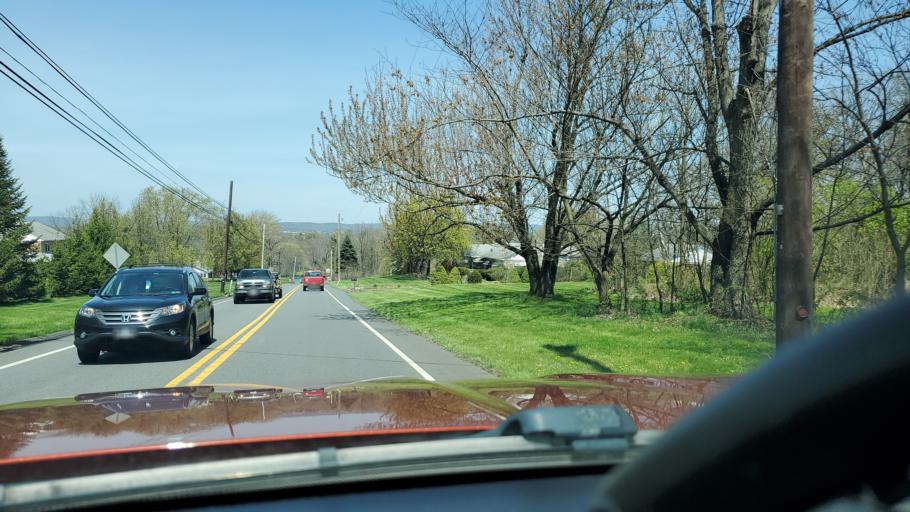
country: US
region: Pennsylvania
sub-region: Montgomery County
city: Pennsburg
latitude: 40.3667
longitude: -75.5223
